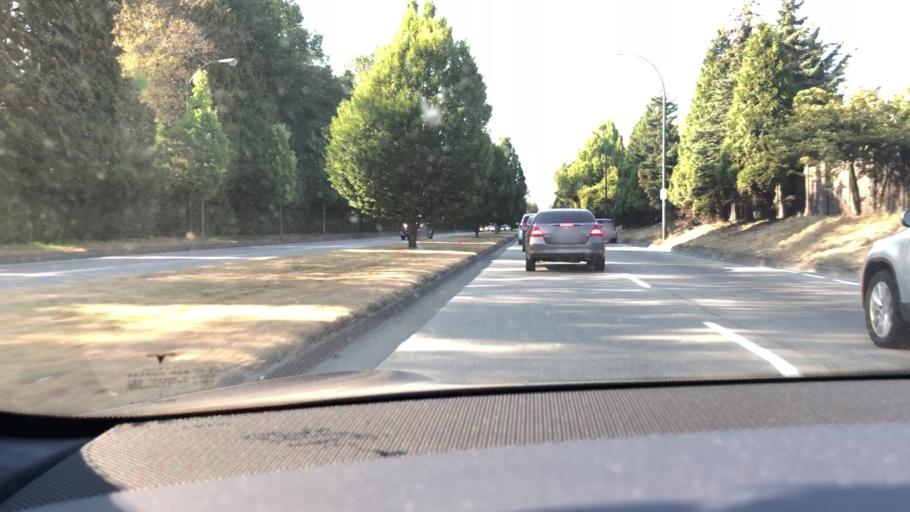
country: CA
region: British Columbia
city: Burnaby
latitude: 49.2179
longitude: -123.0237
